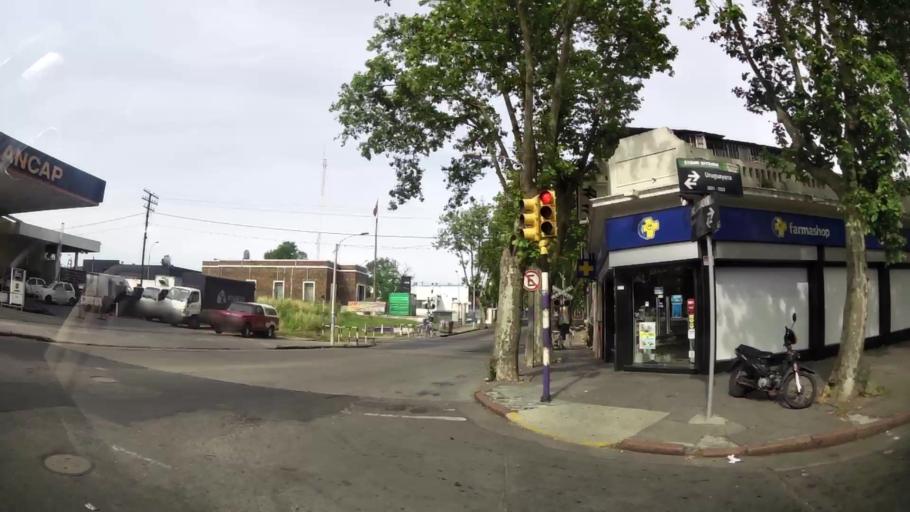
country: UY
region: Montevideo
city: Montevideo
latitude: -34.8699
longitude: -56.2093
